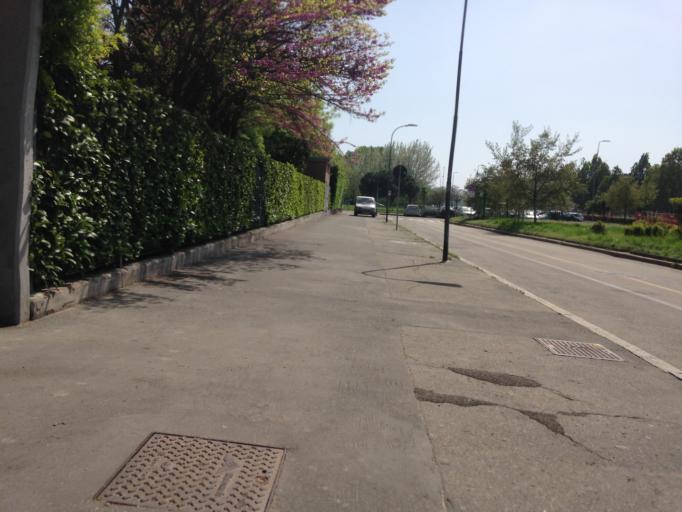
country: IT
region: Lombardy
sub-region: Citta metropolitana di Milano
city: Milano
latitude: 45.4265
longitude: 9.1783
